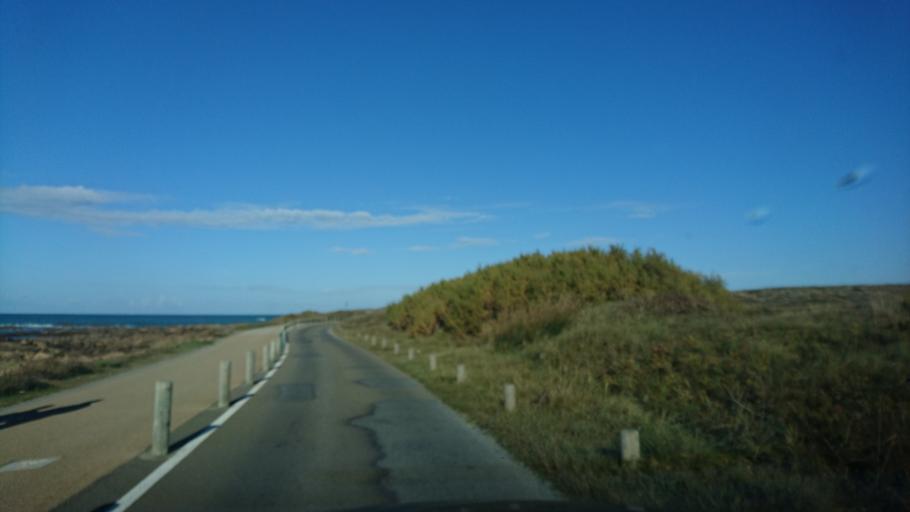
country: FR
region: Pays de la Loire
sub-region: Departement de la Vendee
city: Les Sables-d'Olonne
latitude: 46.5084
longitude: -1.8174
